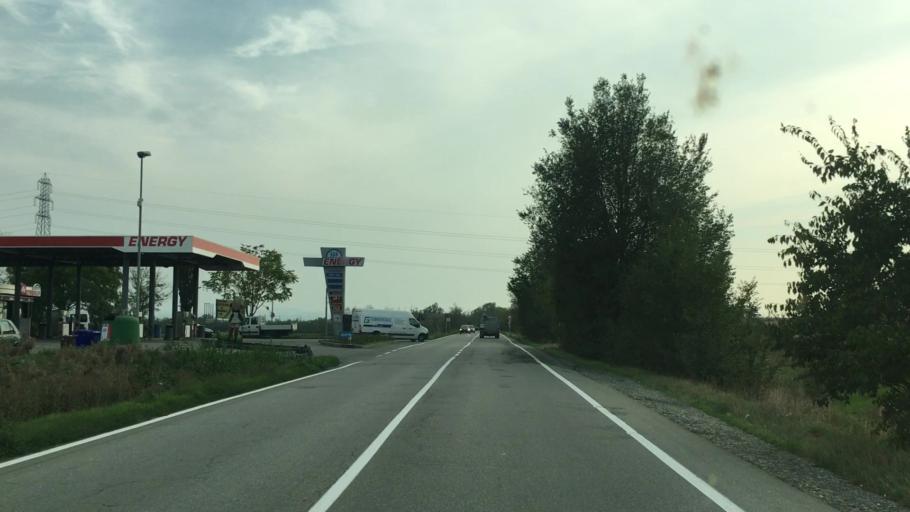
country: IT
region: Emilia-Romagna
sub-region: Provincia di Reggio Emilia
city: Calerno
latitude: 44.7569
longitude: 10.4964
